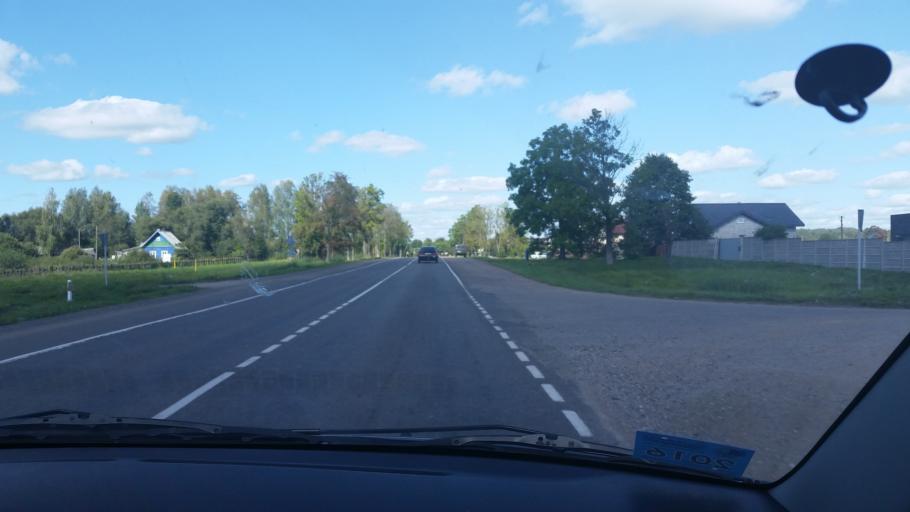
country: BY
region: Vitebsk
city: Vitebsk
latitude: 55.1131
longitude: 30.2826
